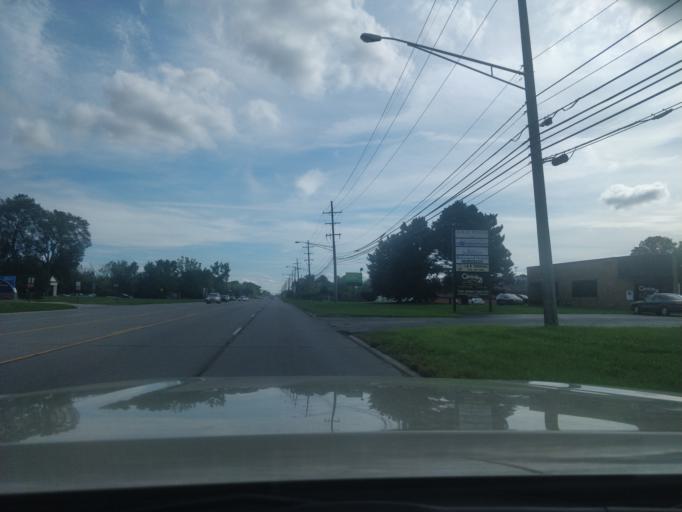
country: US
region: Michigan
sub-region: Wayne County
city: Woodhaven
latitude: 42.1633
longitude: -83.2270
